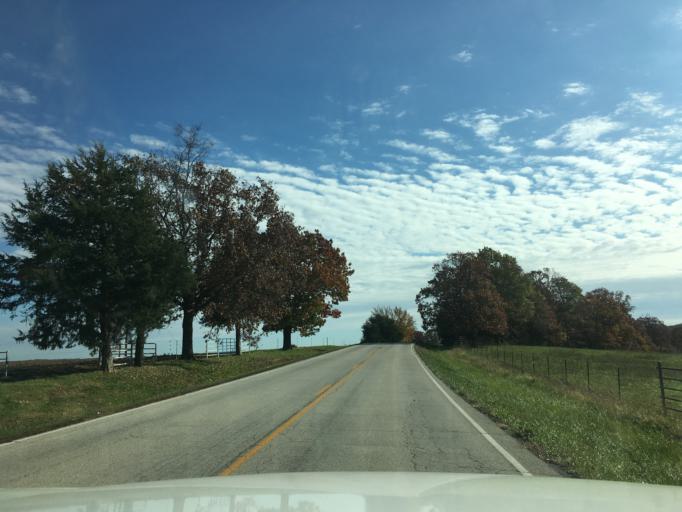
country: US
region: Missouri
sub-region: Maries County
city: Belle
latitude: 38.3478
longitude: -91.7952
